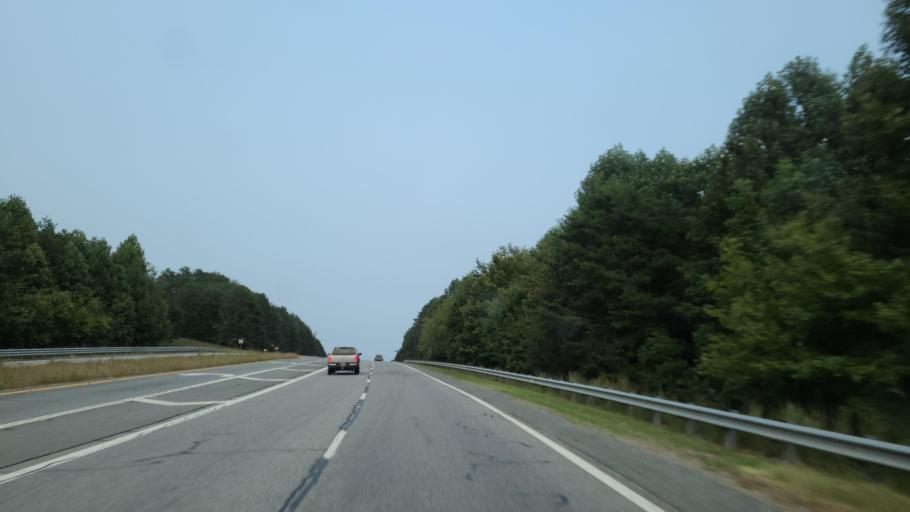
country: US
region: Georgia
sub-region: Fannin County
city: Blue Ridge
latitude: 34.8885
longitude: -84.2060
